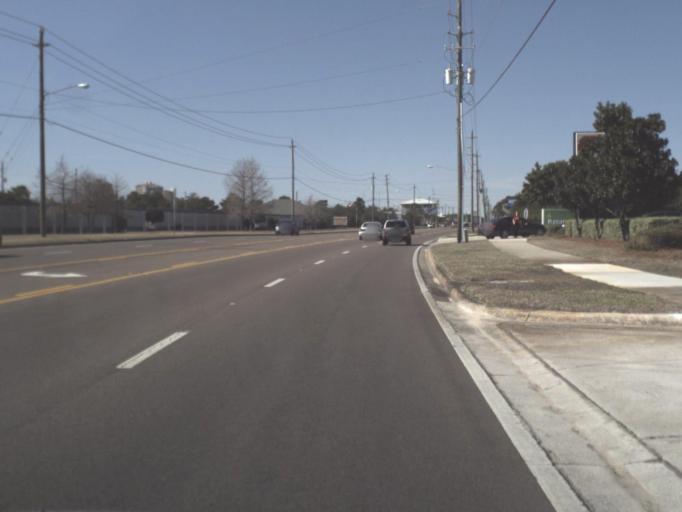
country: US
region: Florida
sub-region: Bay County
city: Panama City Beach
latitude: 30.1843
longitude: -85.8093
